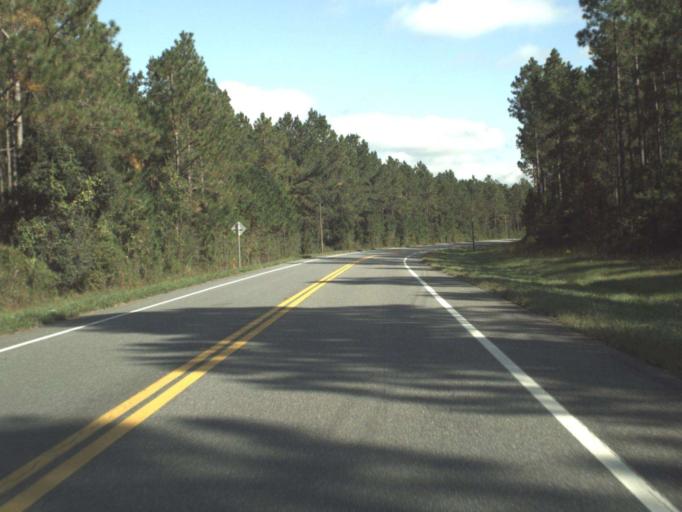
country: US
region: Florida
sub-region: Calhoun County
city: Blountstown
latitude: 30.3283
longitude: -85.1269
